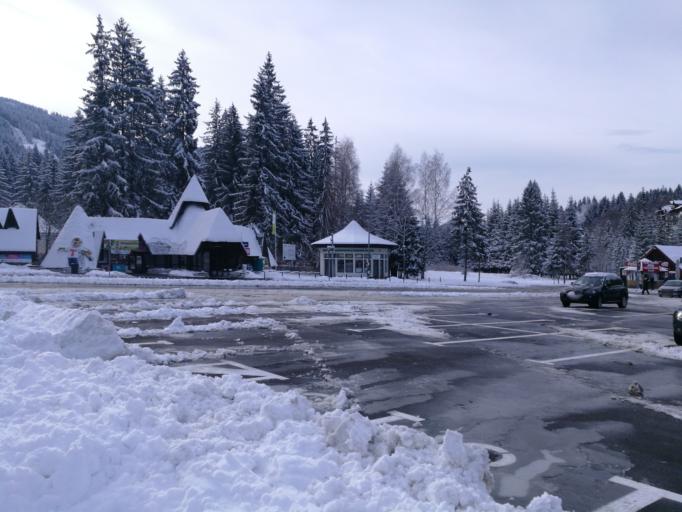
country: RO
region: Brasov
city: Brasov
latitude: 45.5953
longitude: 25.5534
